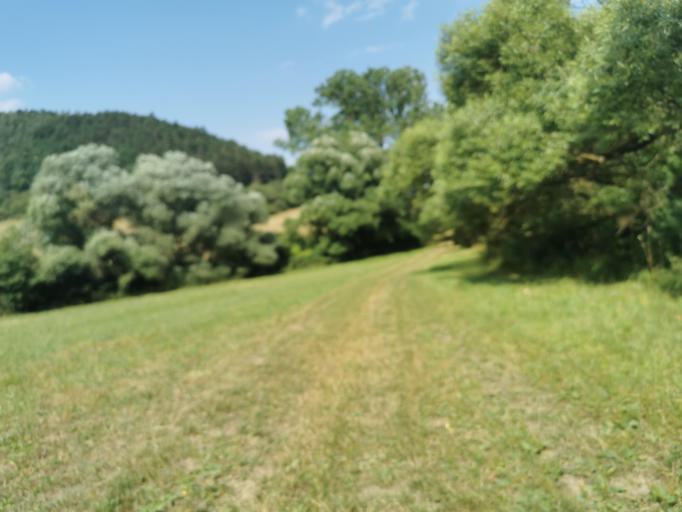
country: SK
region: Trenciansky
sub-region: Okres Myjava
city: Myjava
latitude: 48.7390
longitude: 17.5272
